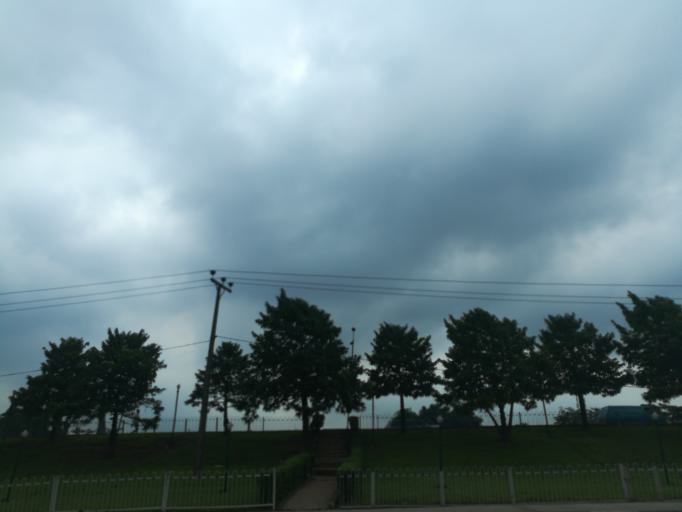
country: NG
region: Lagos
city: Ikeja
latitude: 6.6193
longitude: 3.3642
